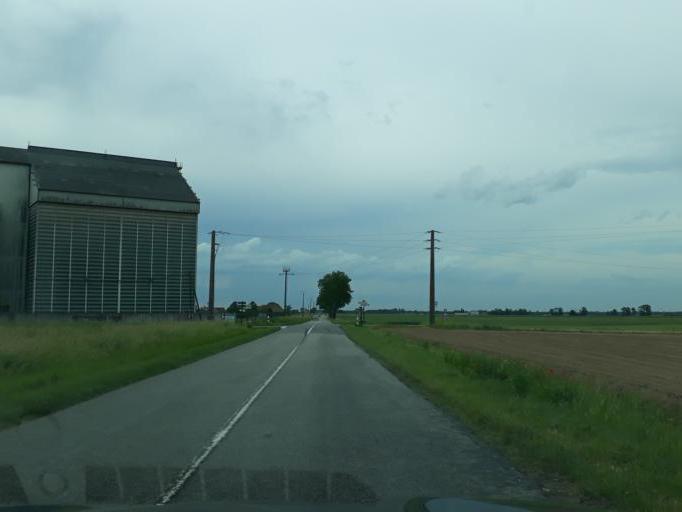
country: FR
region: Centre
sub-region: Departement du Loiret
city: Tigy
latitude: 47.8165
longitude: 2.1687
